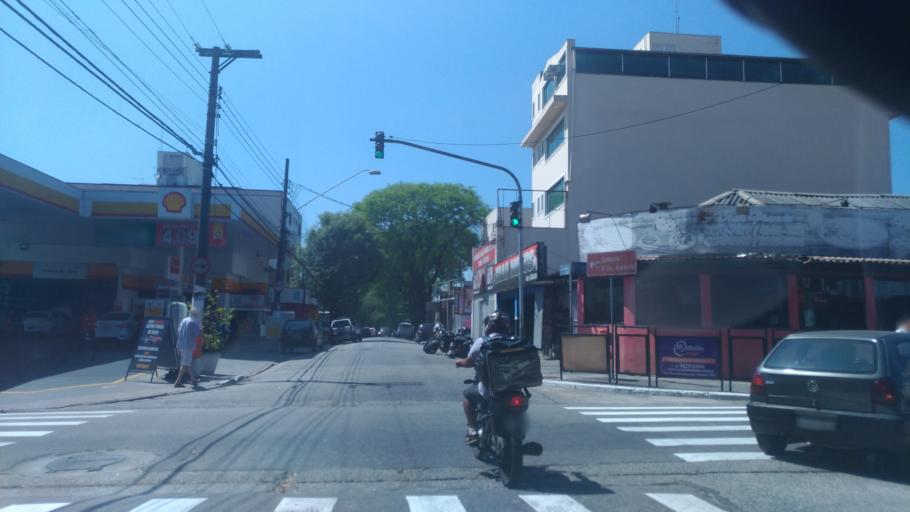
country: BR
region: Sao Paulo
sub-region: Sao Bernardo Do Campo
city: Sao Bernardo do Campo
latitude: -23.6678
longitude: -46.5882
